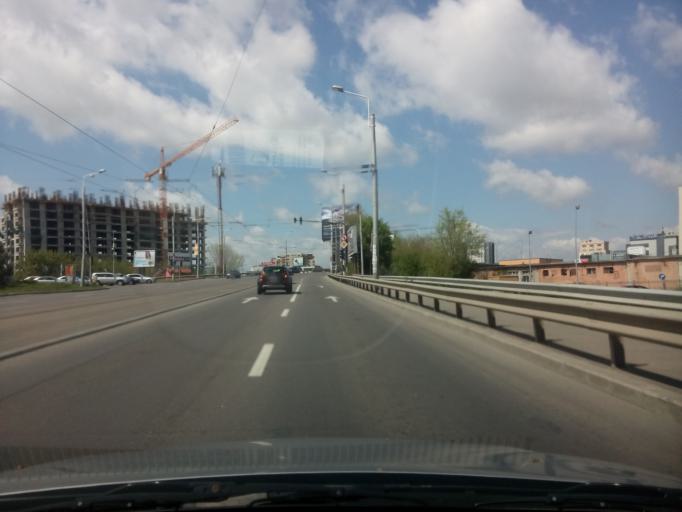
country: RO
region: Bucuresti
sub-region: Municipiul Bucuresti
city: Bucharest
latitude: 44.4870
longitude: 26.0932
